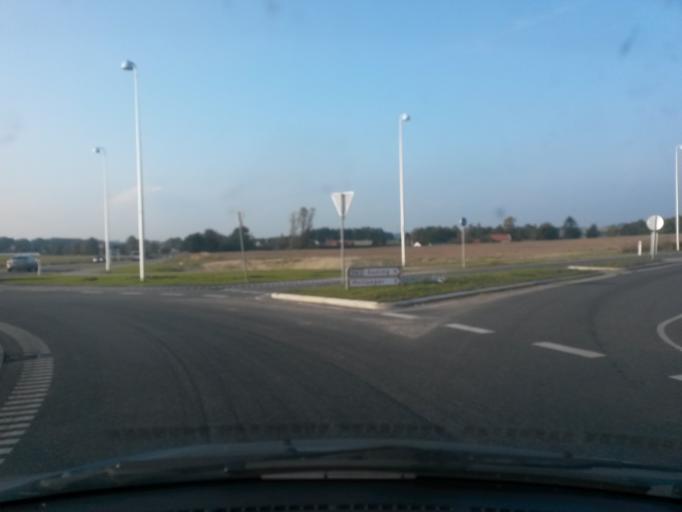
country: DK
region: Central Jutland
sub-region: Syddjurs Kommune
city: Hornslet
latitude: 56.3536
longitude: 10.3466
